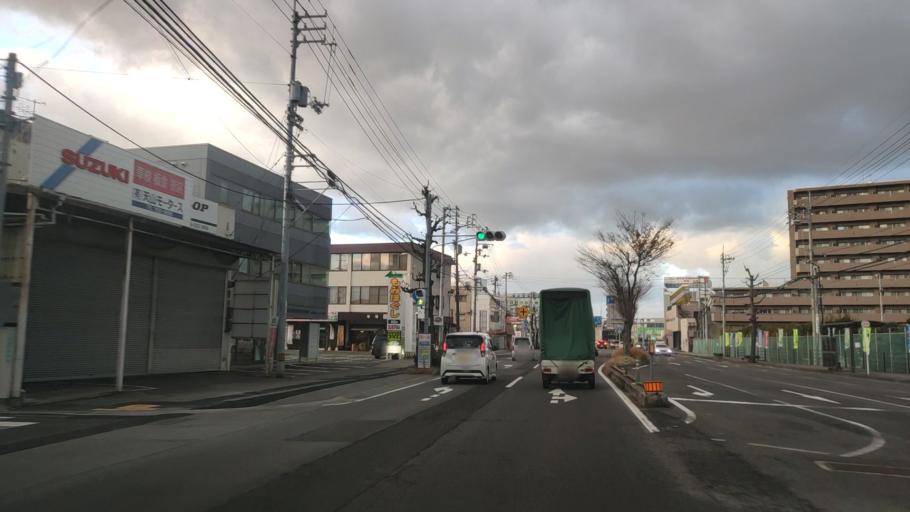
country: JP
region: Ehime
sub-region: Shikoku-chuo Shi
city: Matsuyama
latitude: 33.8206
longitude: 132.7763
